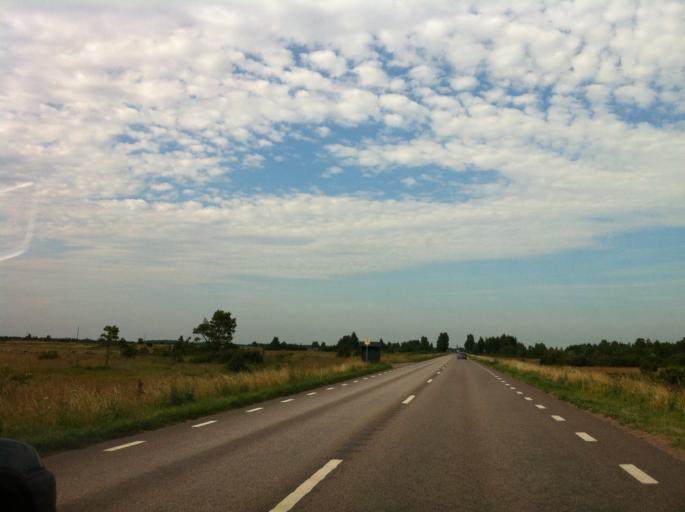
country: SE
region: Kalmar
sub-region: Borgholms Kommun
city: Borgholm
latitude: 56.9276
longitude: 16.7648
